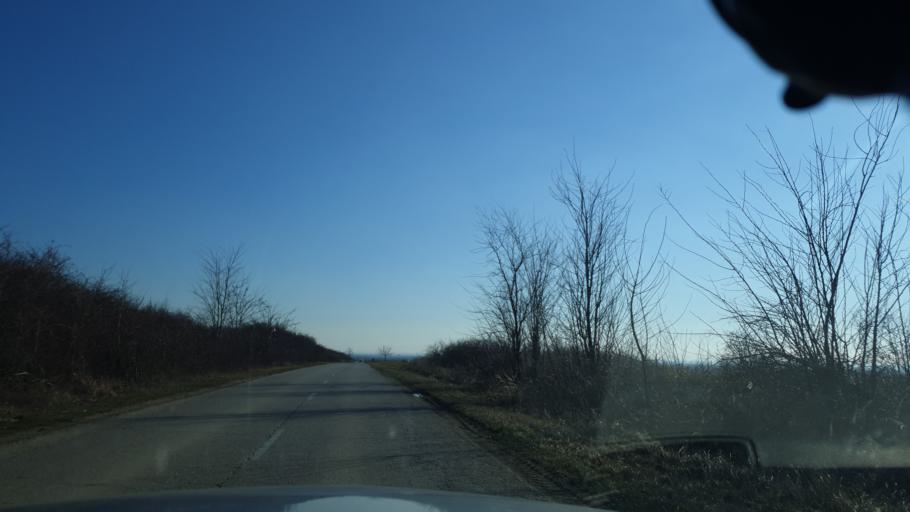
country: RS
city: Vrdnik
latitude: 45.0942
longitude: 19.8054
